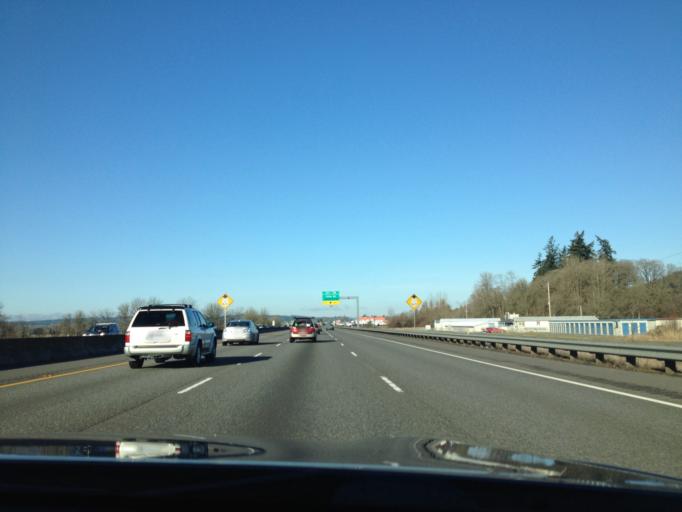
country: US
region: Washington
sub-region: Lewis County
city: Chehalis
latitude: 46.6376
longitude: -122.9462
